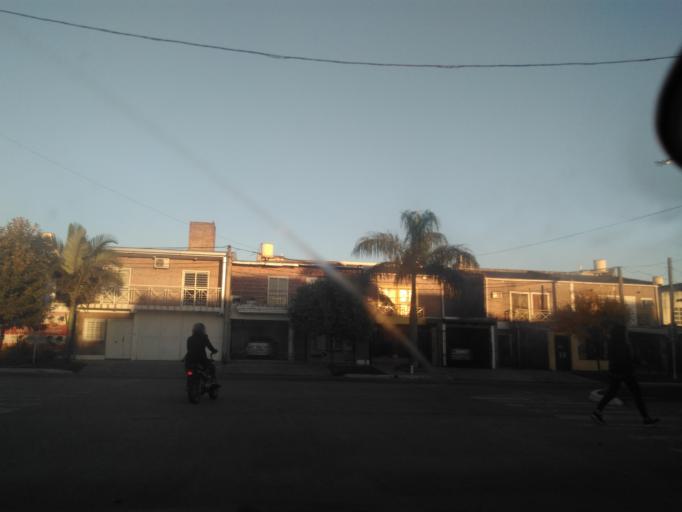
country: AR
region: Chaco
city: Resistencia
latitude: -27.4706
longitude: -58.9866
